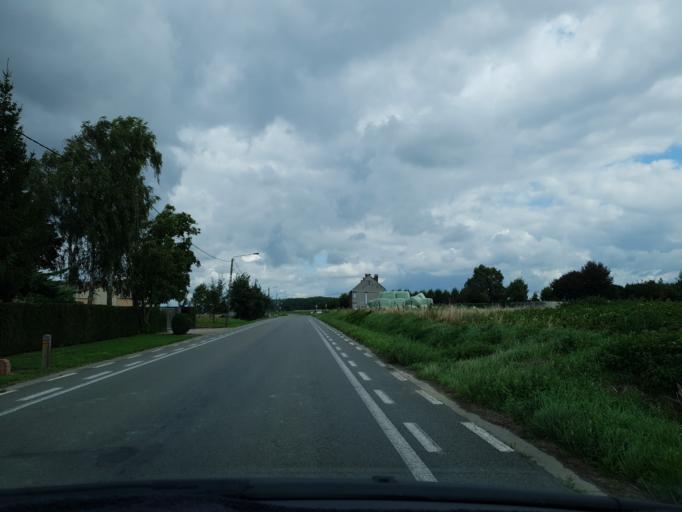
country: BE
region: Wallonia
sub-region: Province du Hainaut
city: Pecq
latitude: 50.7080
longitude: 3.3486
